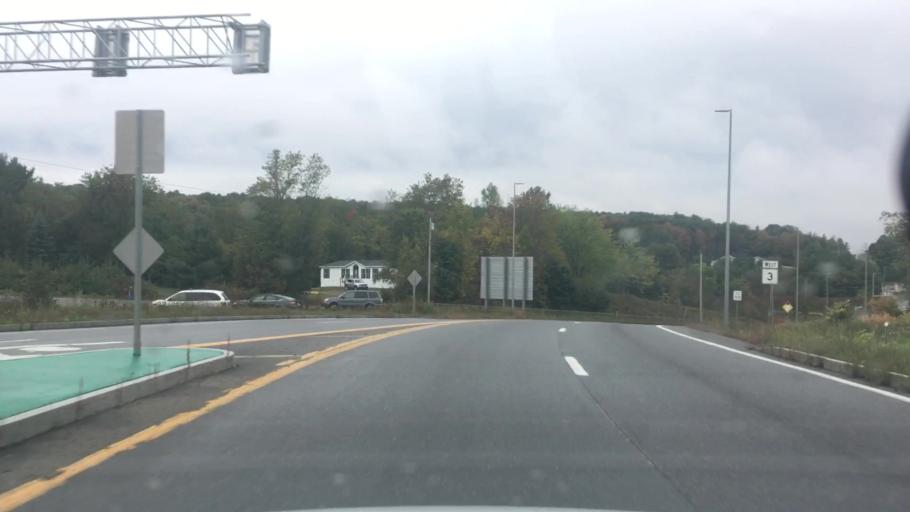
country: US
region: Maine
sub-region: Kennebec County
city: Augusta
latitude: 44.3584
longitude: -69.7848
